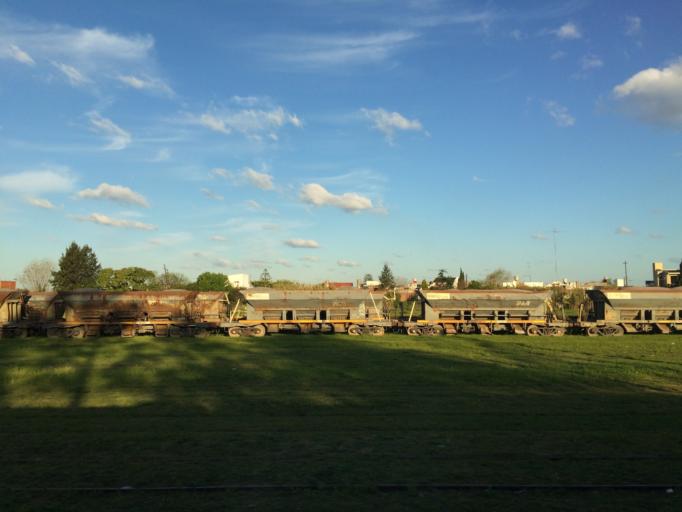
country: AR
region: Buenos Aires
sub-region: Partido de Lanus
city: Lanus
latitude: -34.6854
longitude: -58.3824
